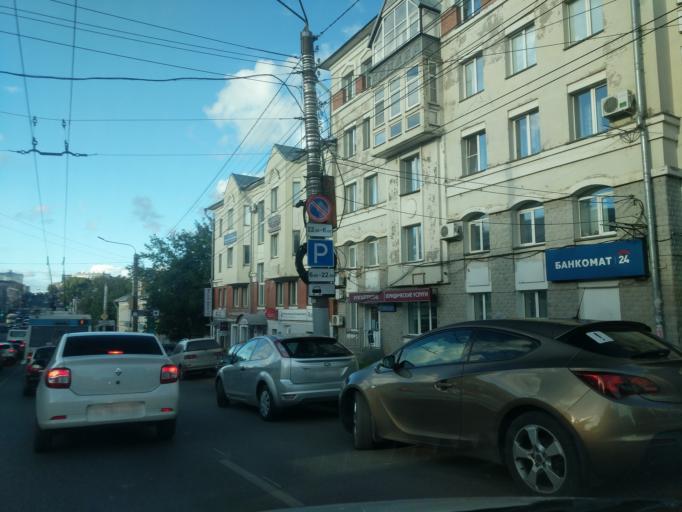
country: RU
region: Kirov
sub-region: Kirovo-Chepetskiy Rayon
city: Kirov
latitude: 58.5988
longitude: 49.6814
